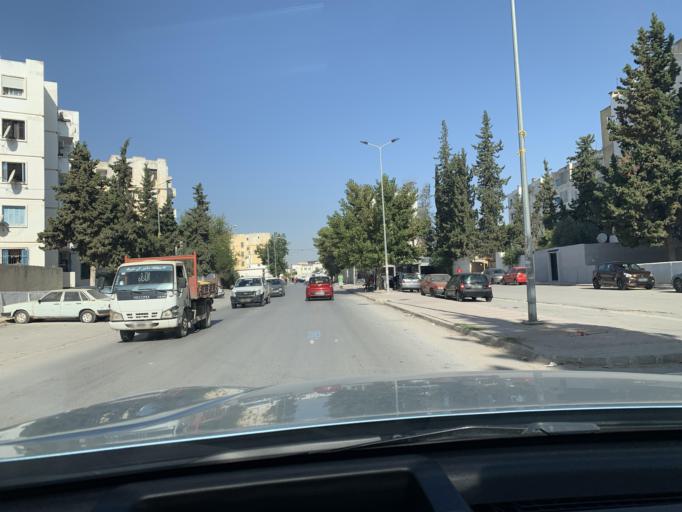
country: TN
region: Manouba
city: Manouba
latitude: 36.8241
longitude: 10.1191
